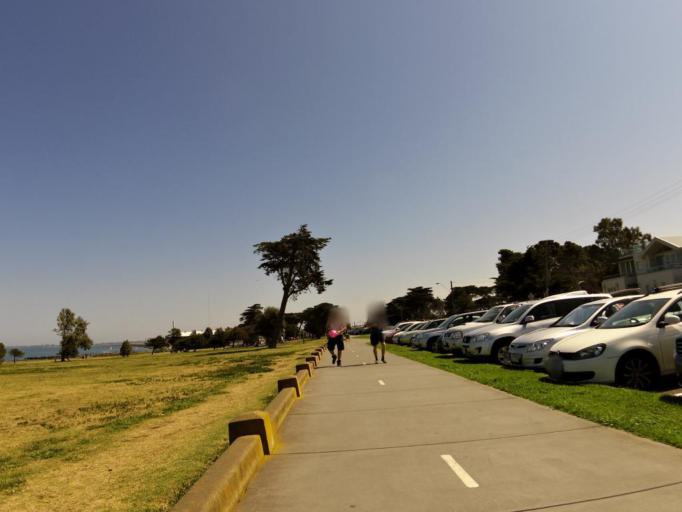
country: AU
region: Victoria
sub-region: Hobsons Bay
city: Williamstown
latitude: -37.8697
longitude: 144.8977
